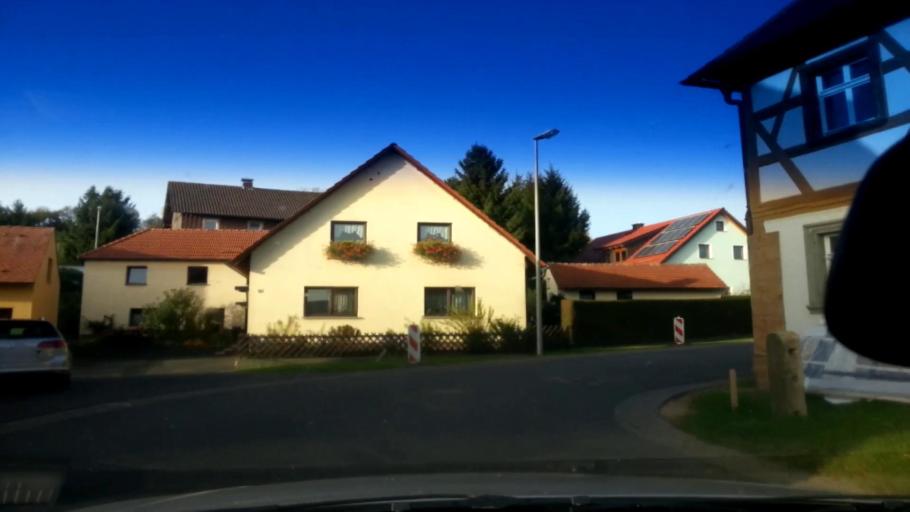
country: DE
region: Bavaria
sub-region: Upper Franconia
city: Schesslitz
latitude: 49.9778
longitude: 11.0293
